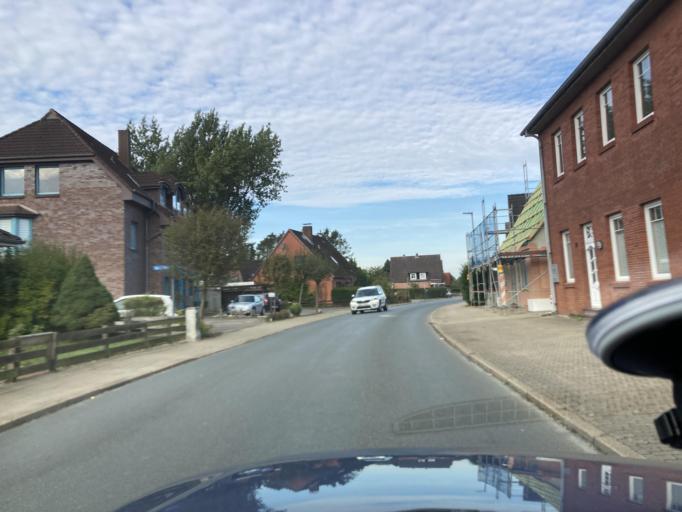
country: DE
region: Schleswig-Holstein
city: Wesseln
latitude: 54.1952
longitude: 9.0826
